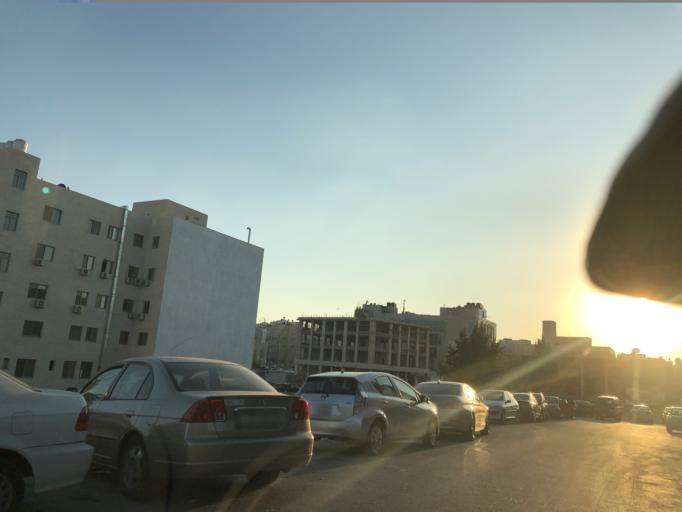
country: JO
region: Amman
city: Wadi as Sir
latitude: 31.9558
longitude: 35.8553
